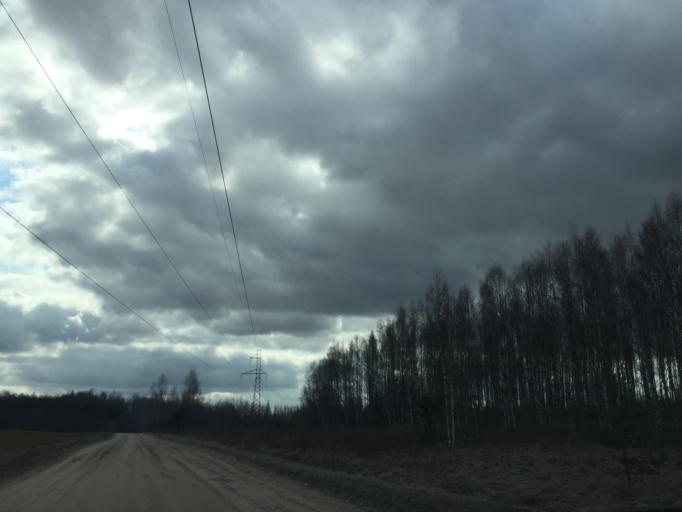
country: LV
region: Vecumnieki
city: Vecumnieki
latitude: 56.5830
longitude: 24.6065
